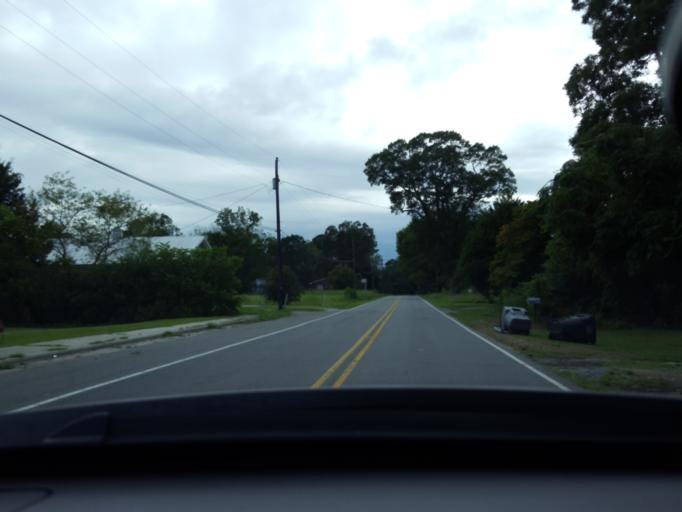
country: US
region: North Carolina
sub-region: Duplin County
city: Rose Hill
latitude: 34.8948
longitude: -78.0610
